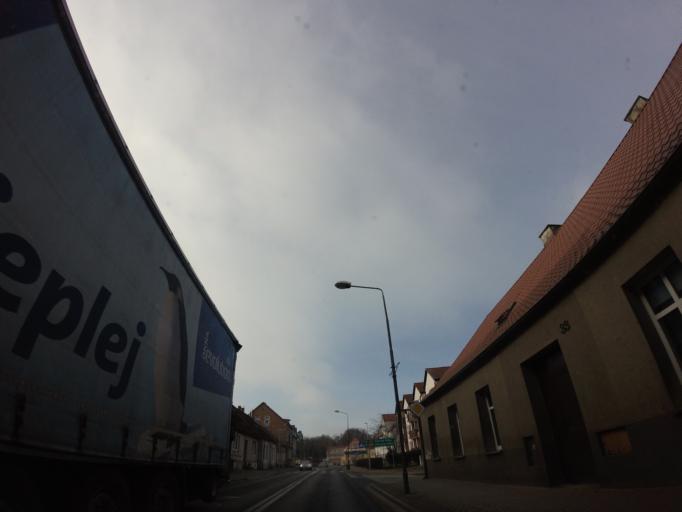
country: PL
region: West Pomeranian Voivodeship
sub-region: Powiat walecki
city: Walcz
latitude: 53.2683
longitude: 16.4633
